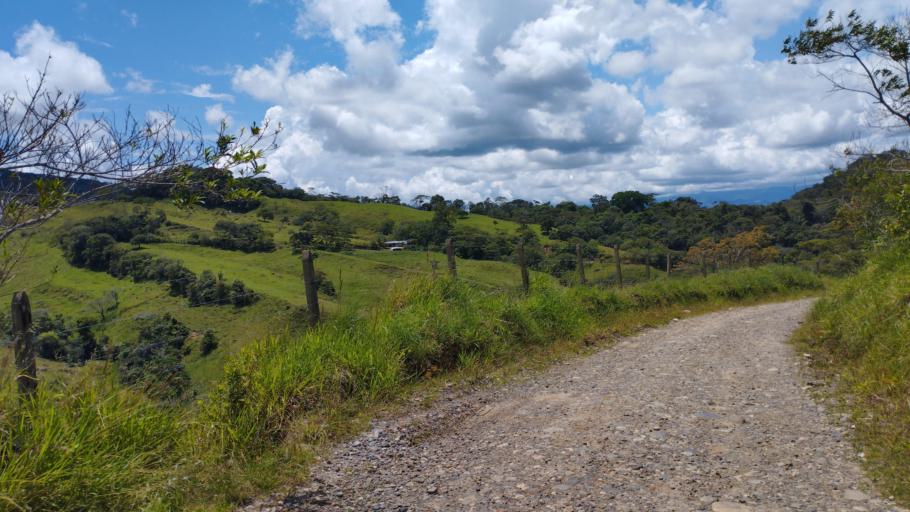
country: CO
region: Boyaca
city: San Luis de Gaceno
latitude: 4.7746
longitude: -73.1323
